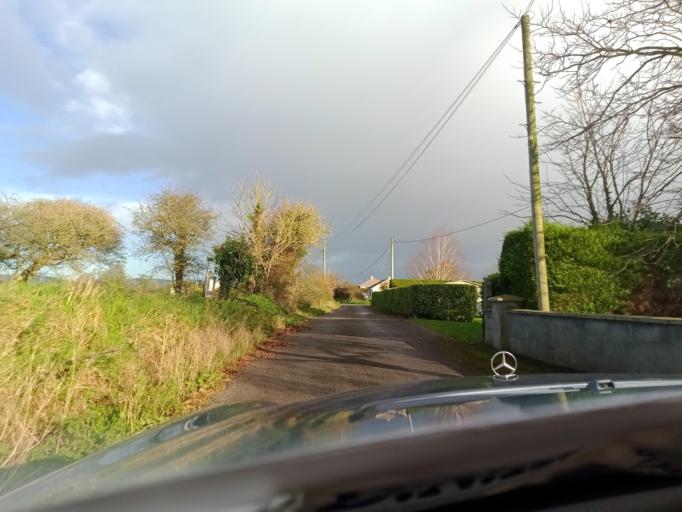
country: IE
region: Leinster
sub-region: Kilkenny
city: Mooncoin
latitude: 52.2985
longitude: -7.2735
